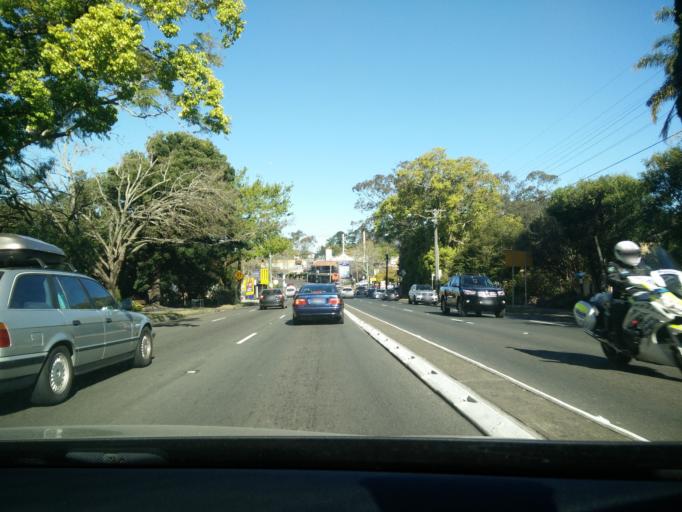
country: AU
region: New South Wales
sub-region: City of Sydney
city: Pymble
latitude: -33.7319
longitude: 151.1258
